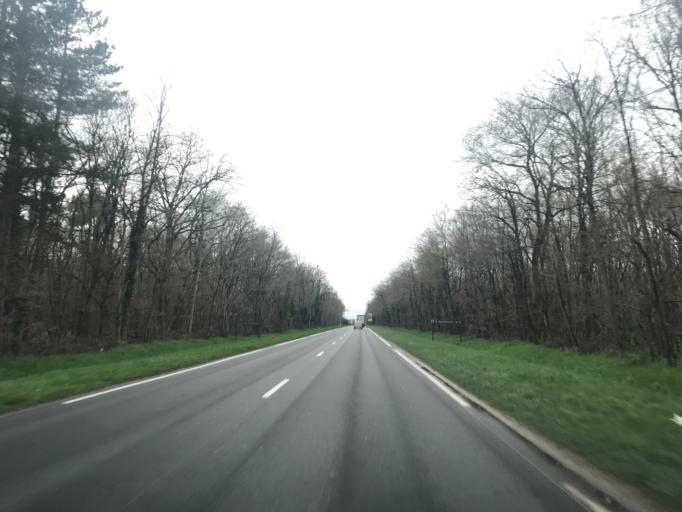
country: FR
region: Centre
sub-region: Departement du Loiret
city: Bray-en-Val
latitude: 47.8400
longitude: 2.3376
